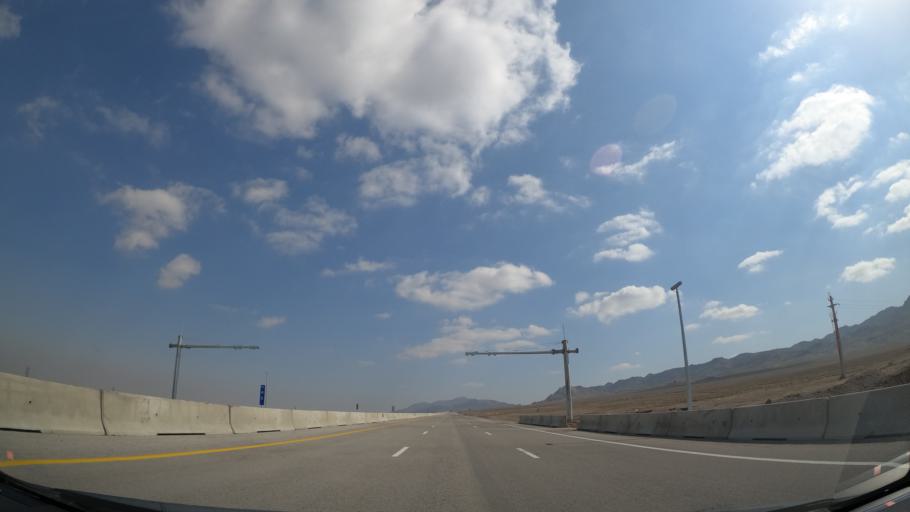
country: IR
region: Alborz
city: Eshtehard
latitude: 35.7145
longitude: 50.5842
